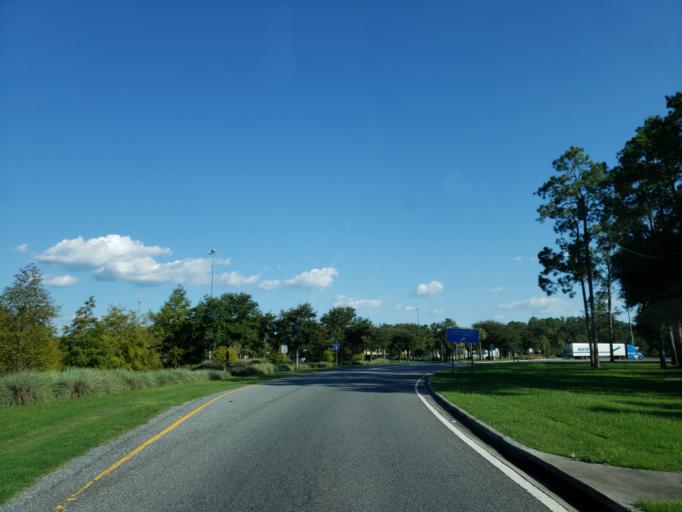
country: US
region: Georgia
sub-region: Echols County
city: Statenville
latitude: 30.6144
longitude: -83.1486
